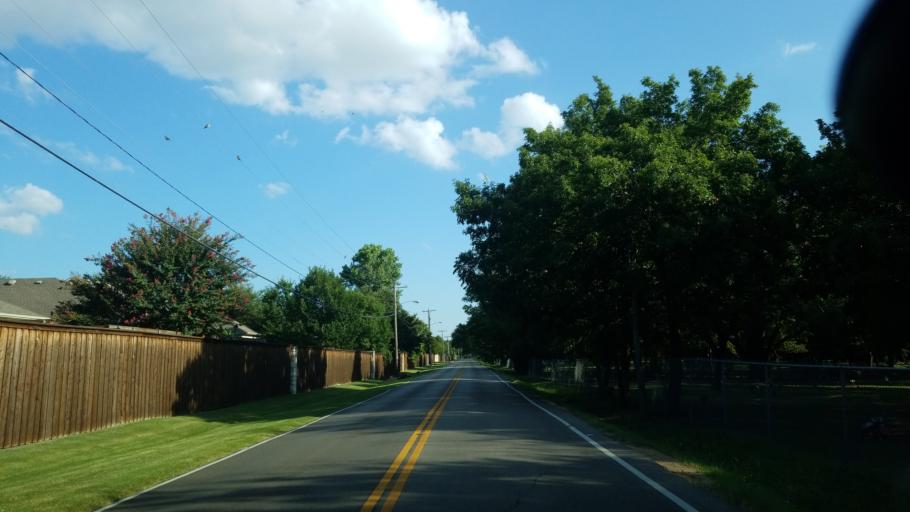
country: US
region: Texas
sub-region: Dallas County
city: Highland Park
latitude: 32.7886
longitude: -96.7172
